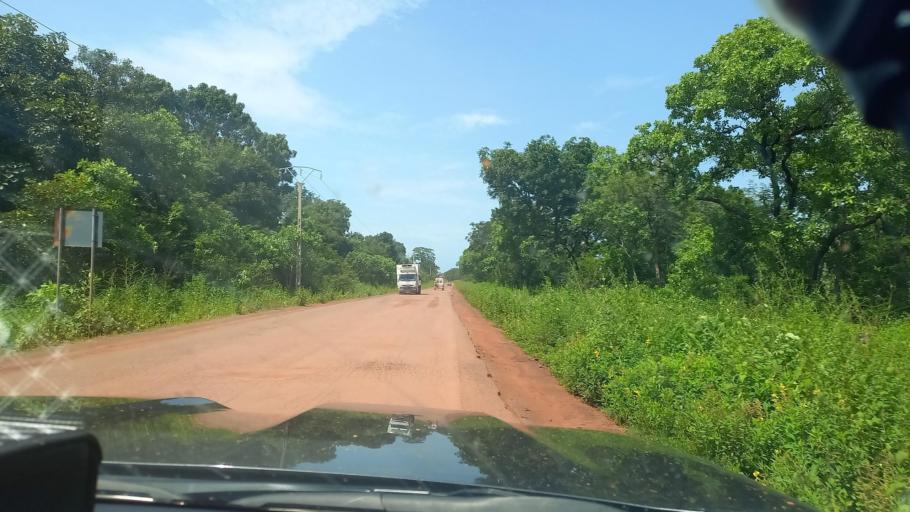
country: SN
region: Kolda
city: Marsassoum
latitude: 12.8576
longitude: -16.0944
